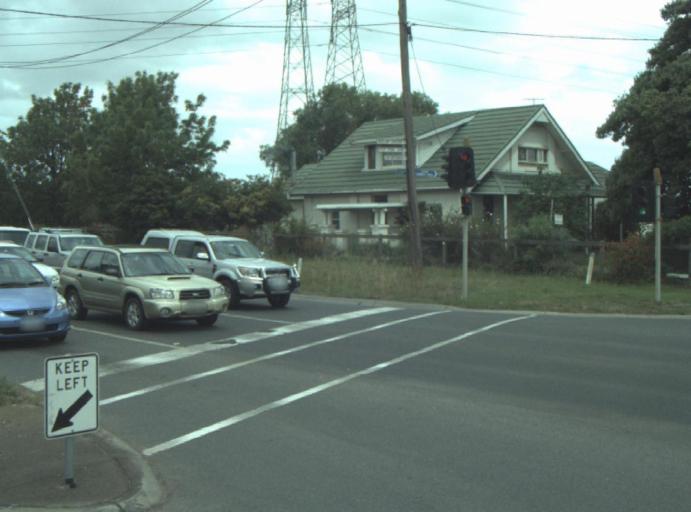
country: AU
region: Victoria
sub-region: Greater Geelong
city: Leopold
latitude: -38.1784
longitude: 144.4203
